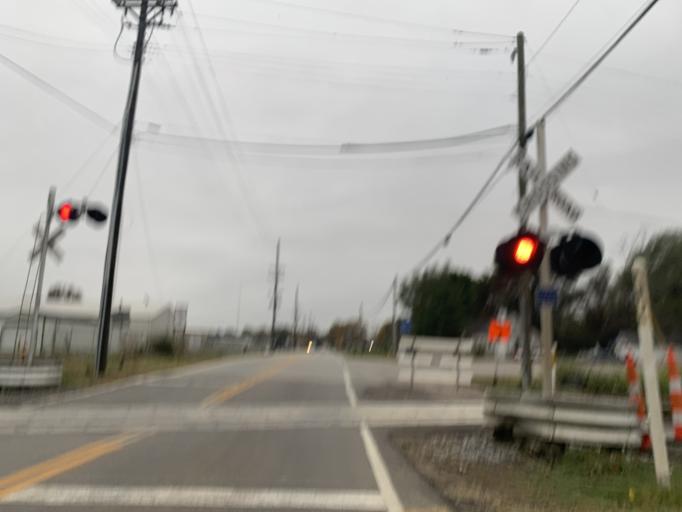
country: US
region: Kentucky
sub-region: Jefferson County
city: Shively
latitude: 38.2147
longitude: -85.8238
